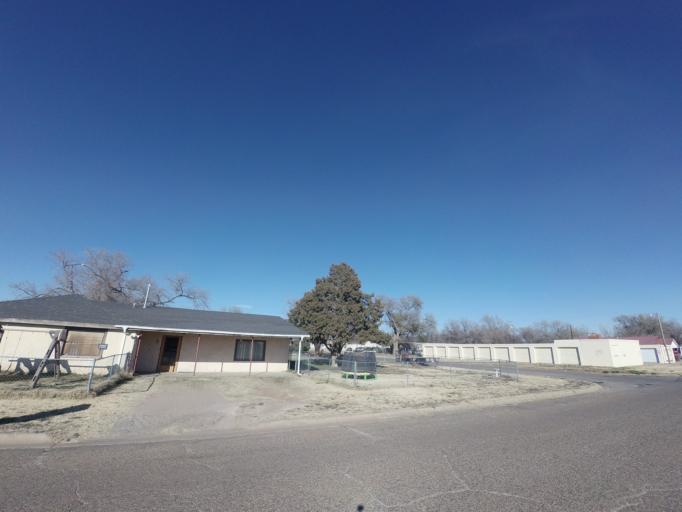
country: US
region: New Mexico
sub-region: Curry County
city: Clovis
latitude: 34.4018
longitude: -103.1843
